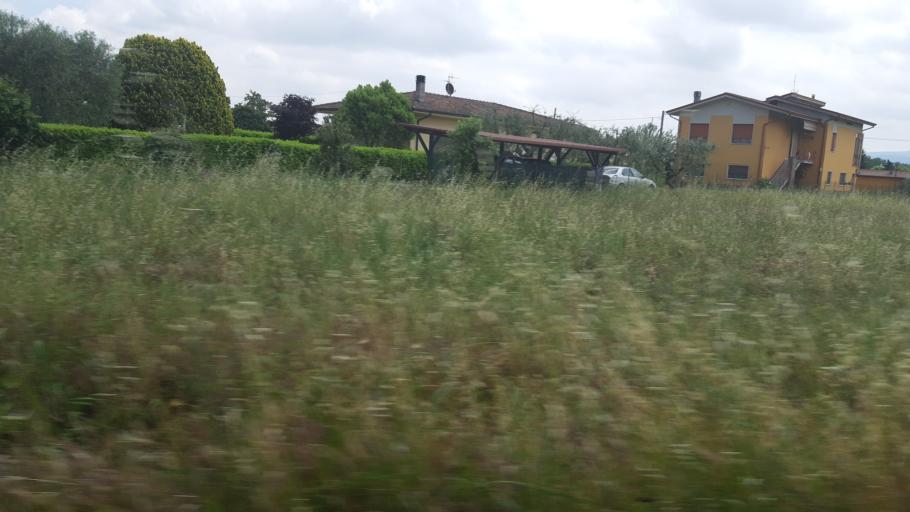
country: IT
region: Tuscany
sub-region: Provincia di Lucca
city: Capannori
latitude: 43.8621
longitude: 10.5515
